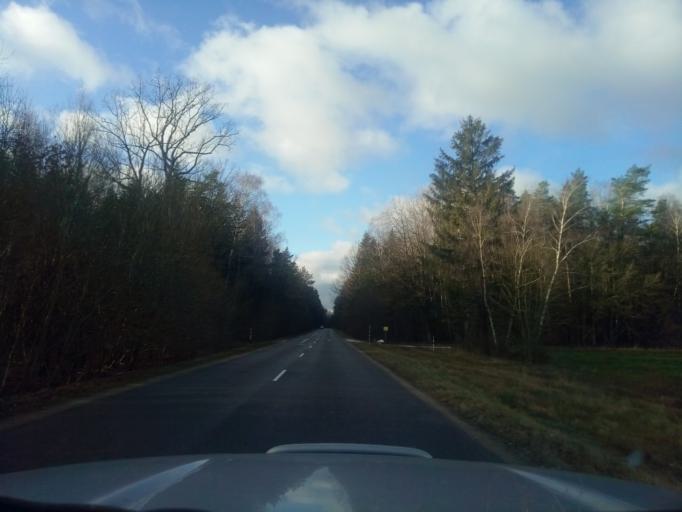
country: BY
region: Minsk
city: Kapyl'
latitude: 53.1755
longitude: 26.9950
